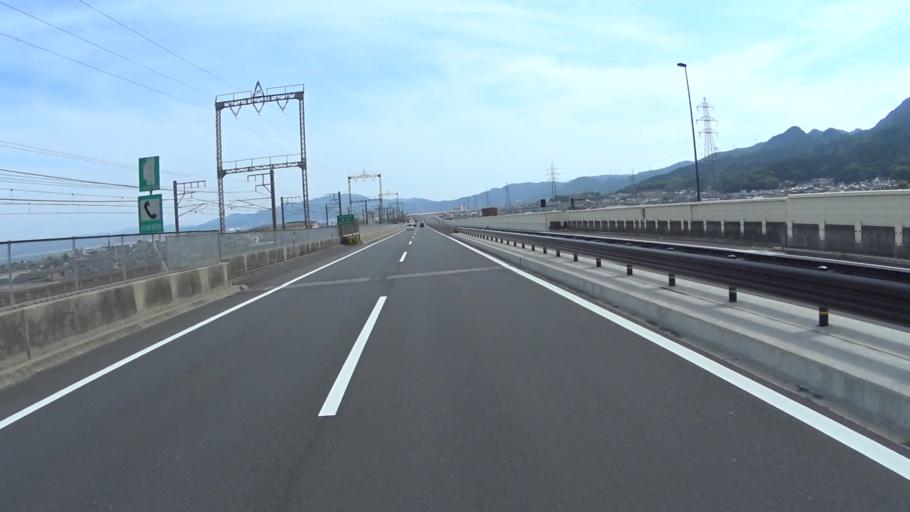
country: JP
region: Shiga Prefecture
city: Otsu-shi
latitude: 35.0692
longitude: 135.8775
